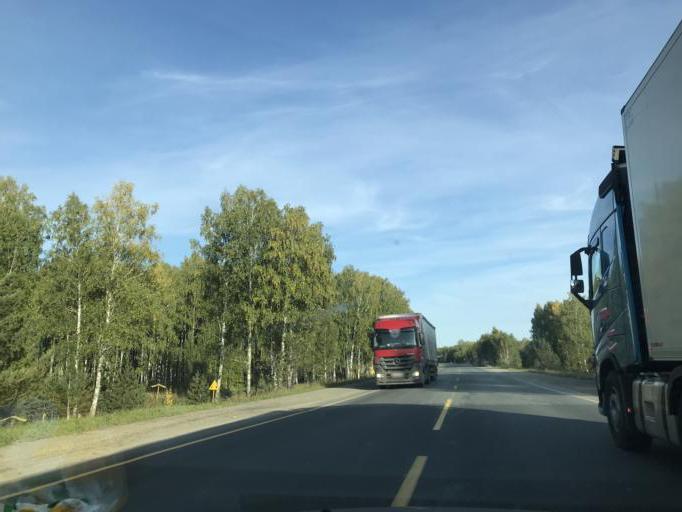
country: RU
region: Chelyabinsk
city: Sargazy
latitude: 54.9715
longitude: 61.2192
